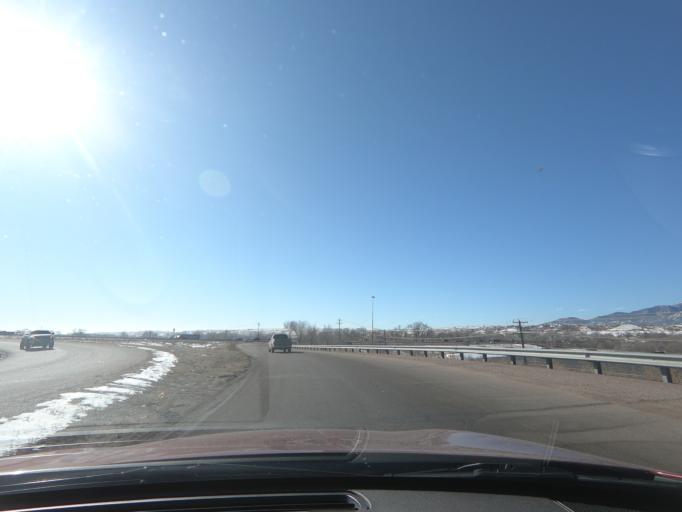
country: US
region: Colorado
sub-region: El Paso County
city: Stratmoor
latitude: 38.7682
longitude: -104.7635
